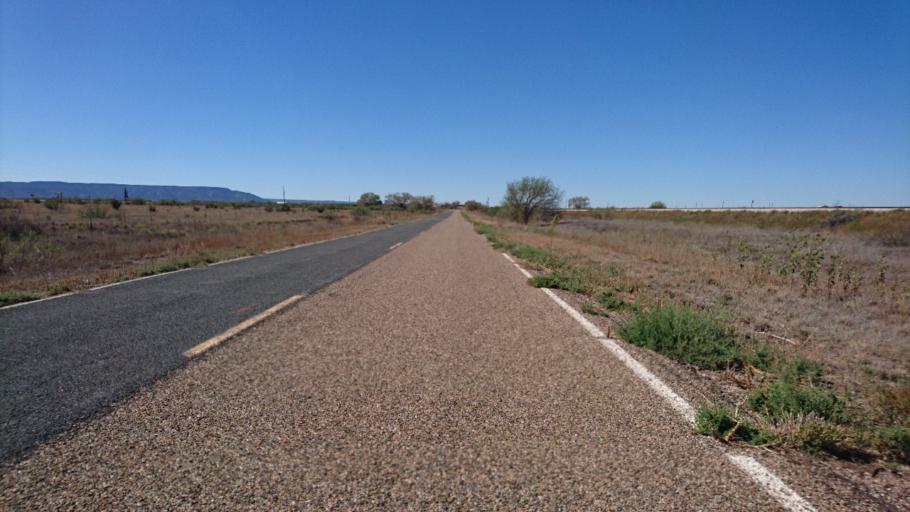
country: US
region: New Mexico
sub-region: Quay County
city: Tucumcari
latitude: 35.0983
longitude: -104.0568
